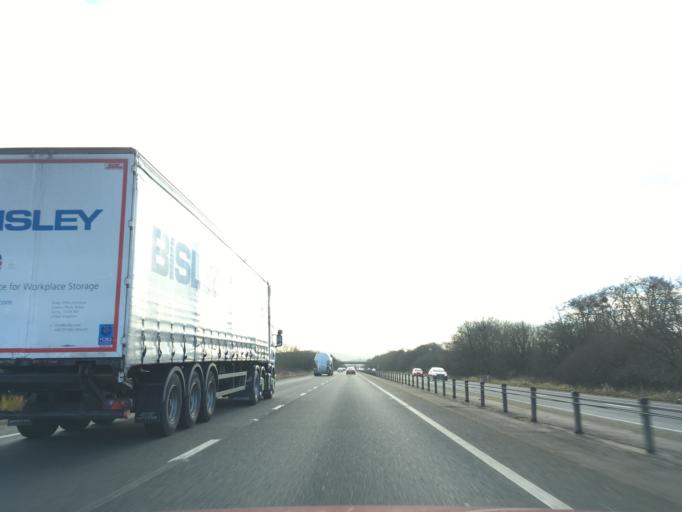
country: GB
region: Wales
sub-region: Monmouthshire
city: Llangwm
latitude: 51.7488
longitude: -2.8420
